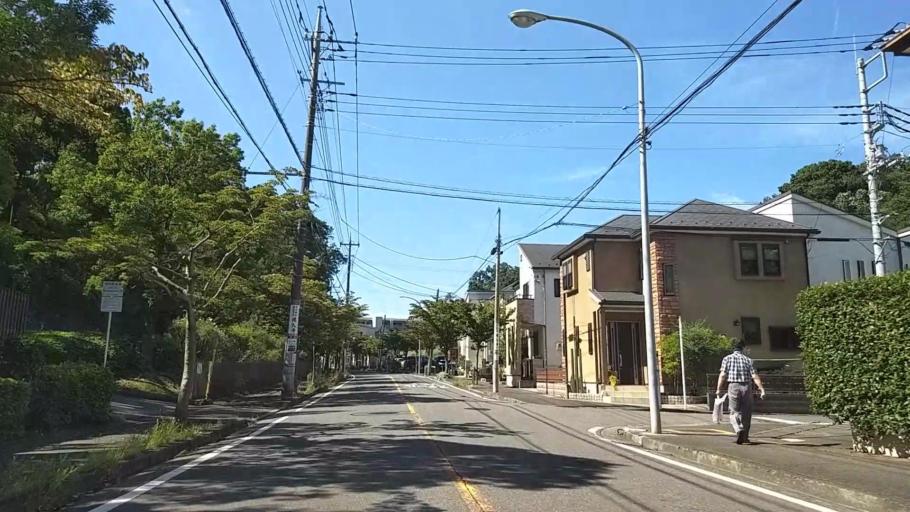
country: JP
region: Tokyo
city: Chofugaoka
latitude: 35.5734
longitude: 139.5401
